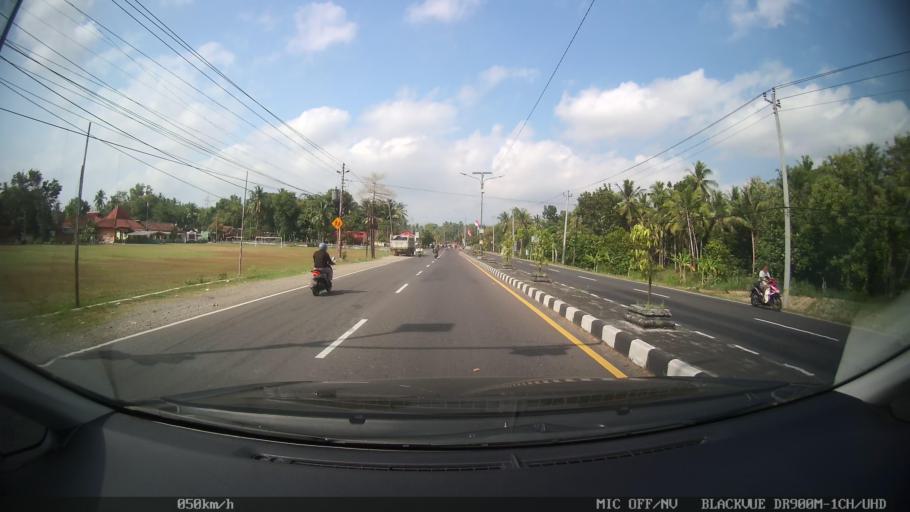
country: ID
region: Daerah Istimewa Yogyakarta
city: Srandakan
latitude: -7.8578
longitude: 110.2128
